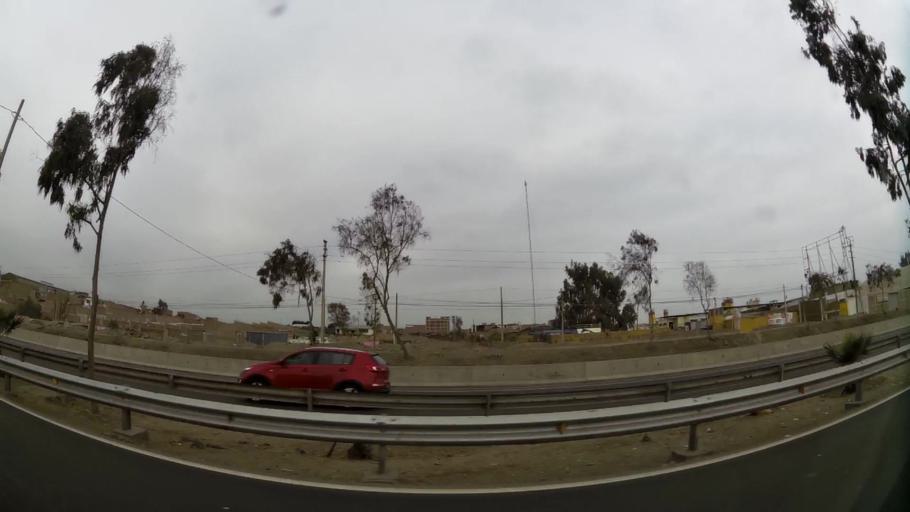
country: PE
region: Lima
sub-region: Lima
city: Surco
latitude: -12.1993
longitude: -76.9737
